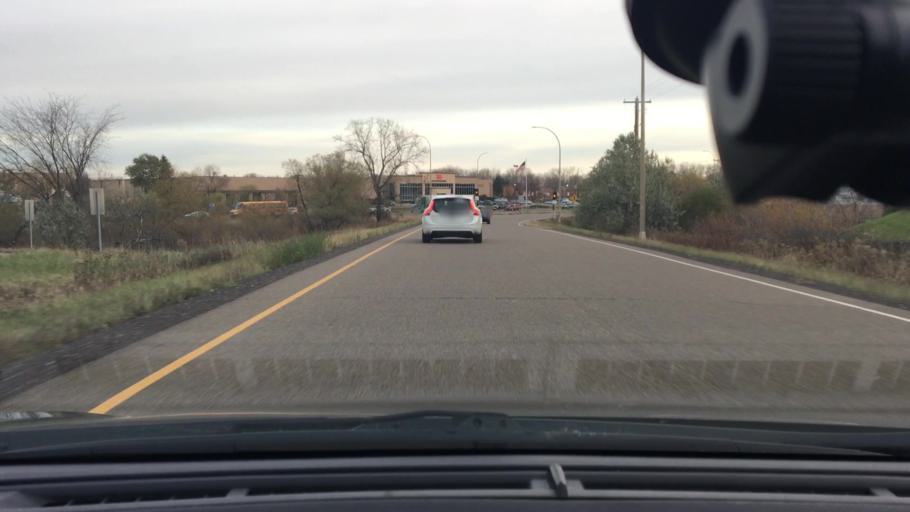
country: US
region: Minnesota
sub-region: Hennepin County
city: New Hope
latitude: 45.0569
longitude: -93.4025
